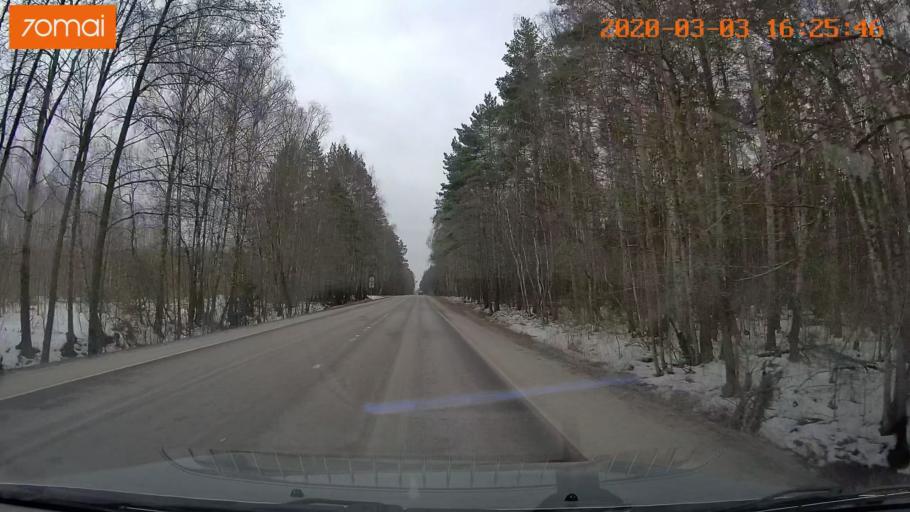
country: RU
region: Moskovskaya
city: Konobeyevo
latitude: 55.4478
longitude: 38.6596
